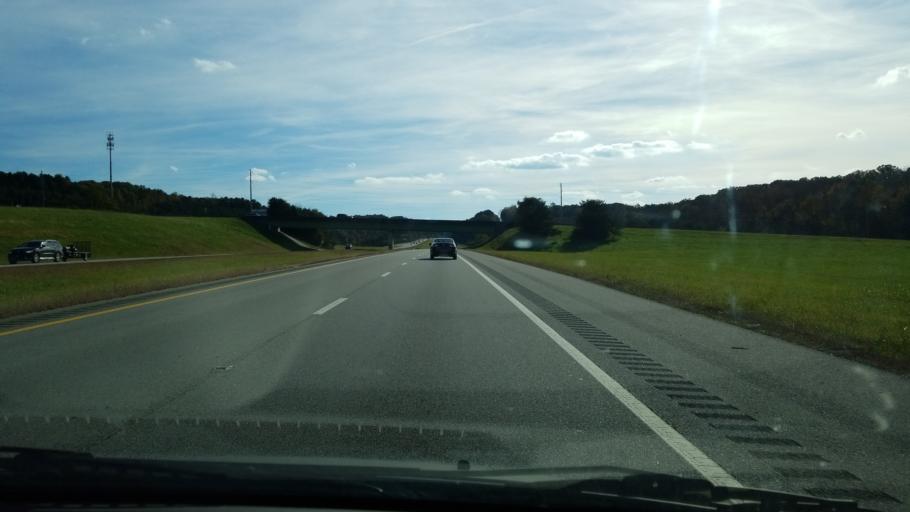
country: US
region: Tennessee
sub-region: Hamilton County
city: Soddy-Daisy
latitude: 35.2790
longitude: -85.1548
